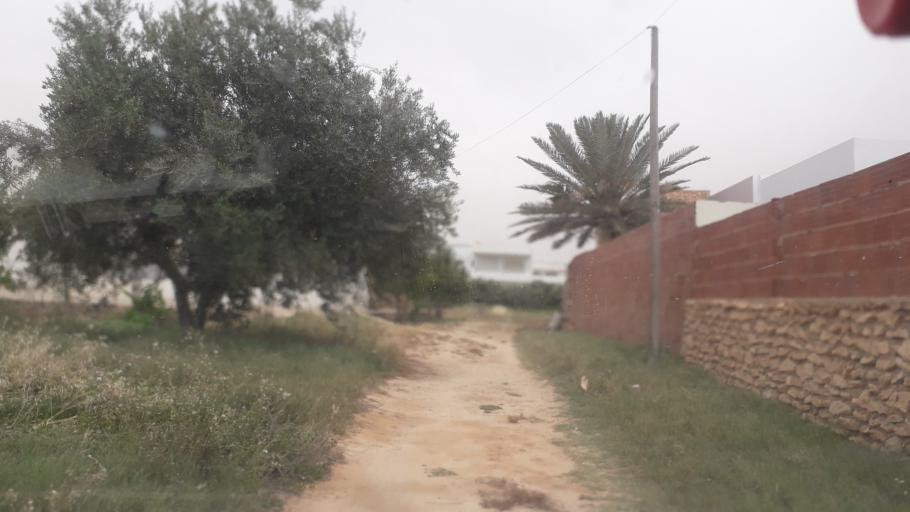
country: TN
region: Safaqis
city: Al Qarmadah
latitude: 34.7947
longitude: 10.7649
